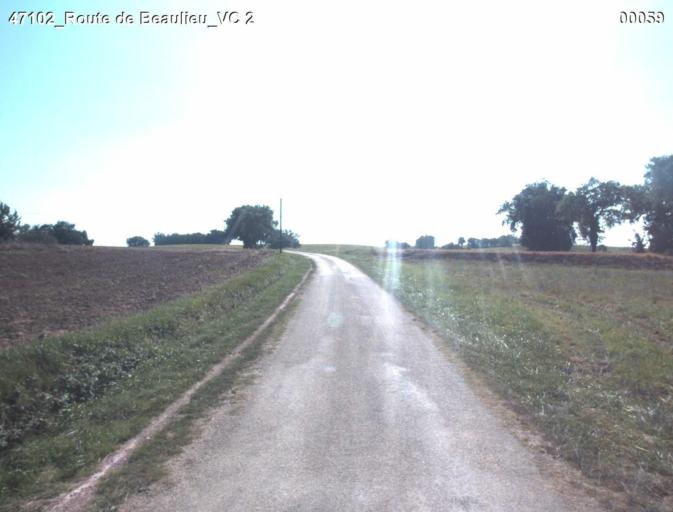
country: FR
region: Aquitaine
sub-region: Departement du Lot-et-Garonne
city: Laplume
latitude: 44.0852
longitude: 0.4470
